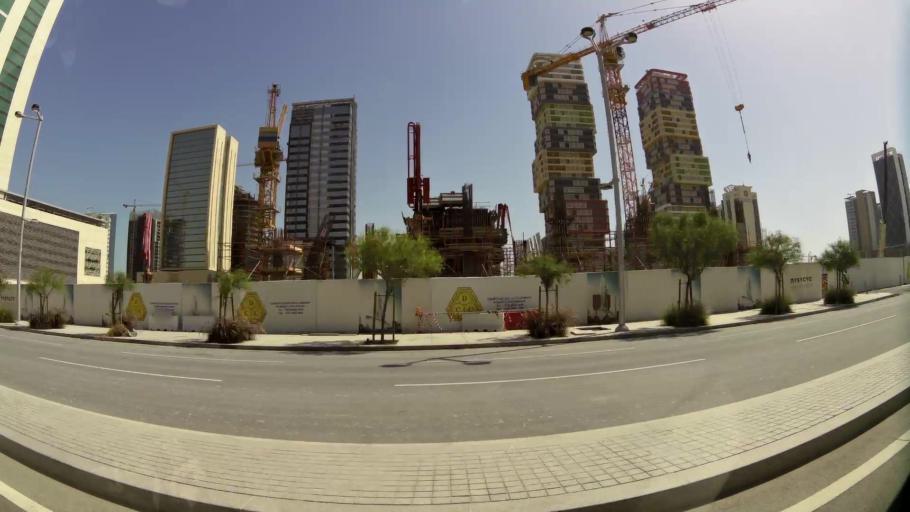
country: QA
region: Baladiyat ad Dawhah
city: Doha
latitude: 25.3875
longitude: 51.5207
